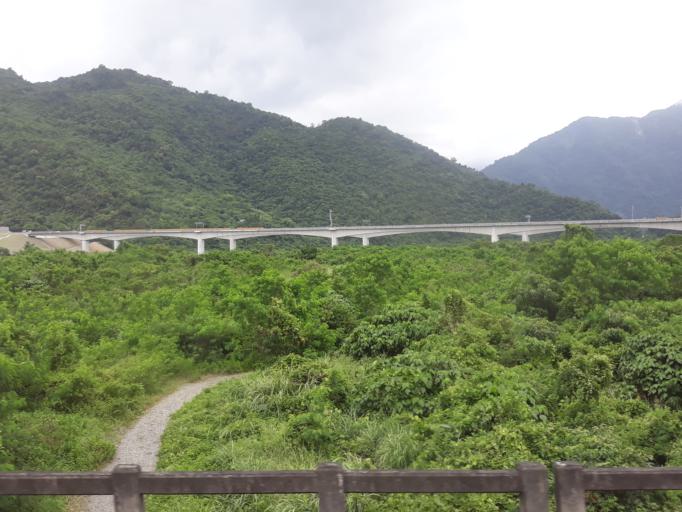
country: TW
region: Taiwan
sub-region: Yilan
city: Yilan
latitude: 24.4428
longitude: 121.7789
